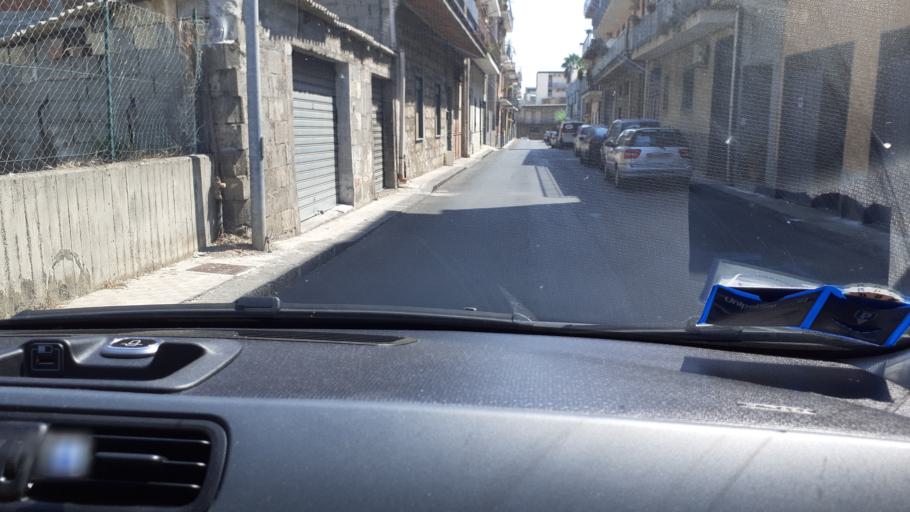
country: IT
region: Sicily
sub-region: Catania
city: Misterbianco
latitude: 37.5180
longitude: 15.0145
